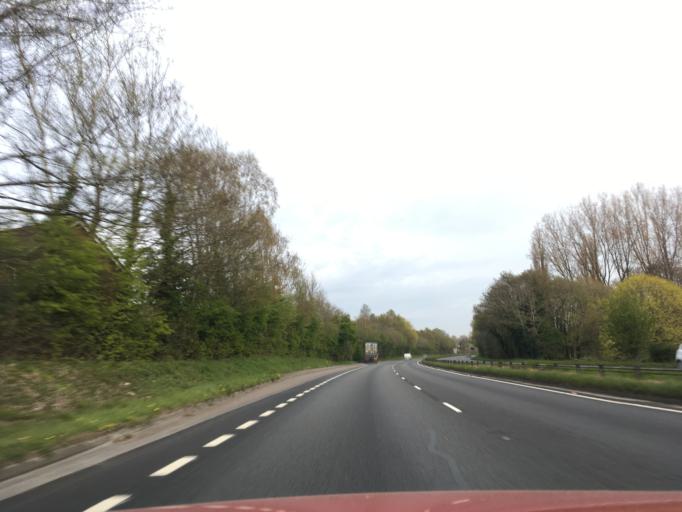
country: GB
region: Wales
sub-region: Caerphilly County Borough
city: Risca
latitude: 51.5922
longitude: -3.0664
